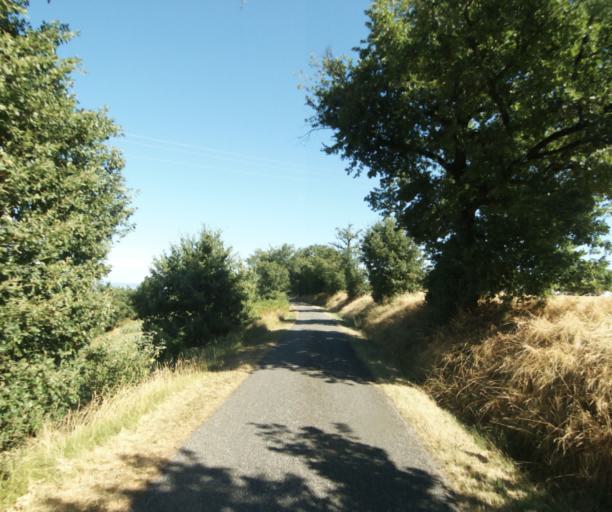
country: FR
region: Midi-Pyrenees
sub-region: Departement de la Haute-Garonne
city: Saint-Felix-Lauragais
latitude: 43.5237
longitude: 1.9071
